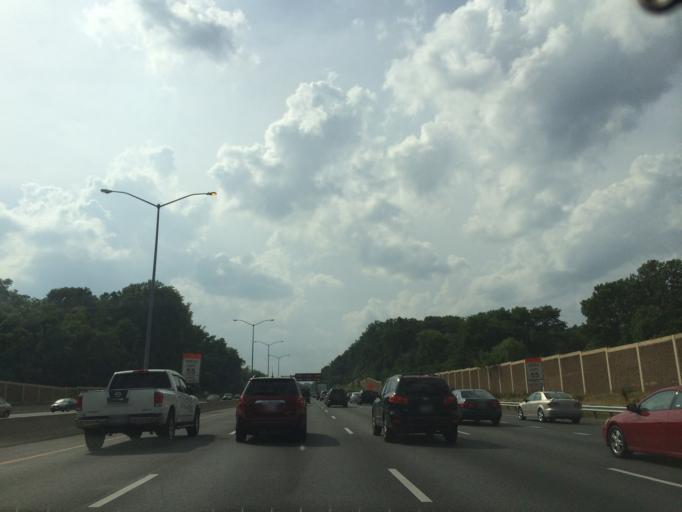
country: US
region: Maryland
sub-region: Baltimore County
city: Charlestown
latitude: 39.2645
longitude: -76.7105
